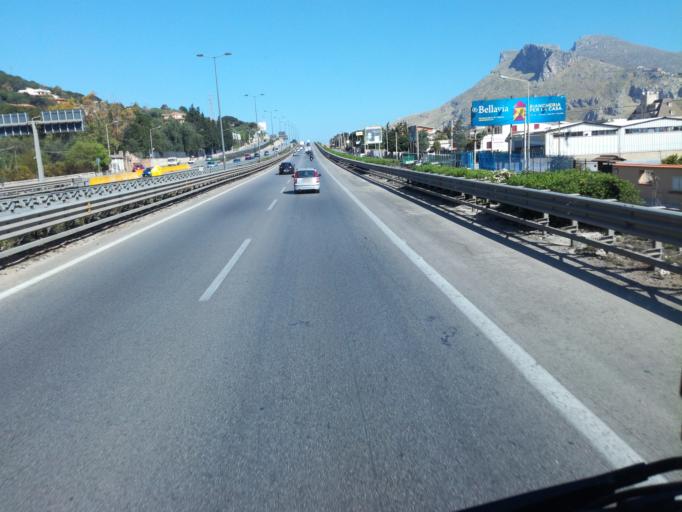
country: IT
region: Sicily
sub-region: Palermo
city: Isola delle Femmine
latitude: 38.1798
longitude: 13.2929
